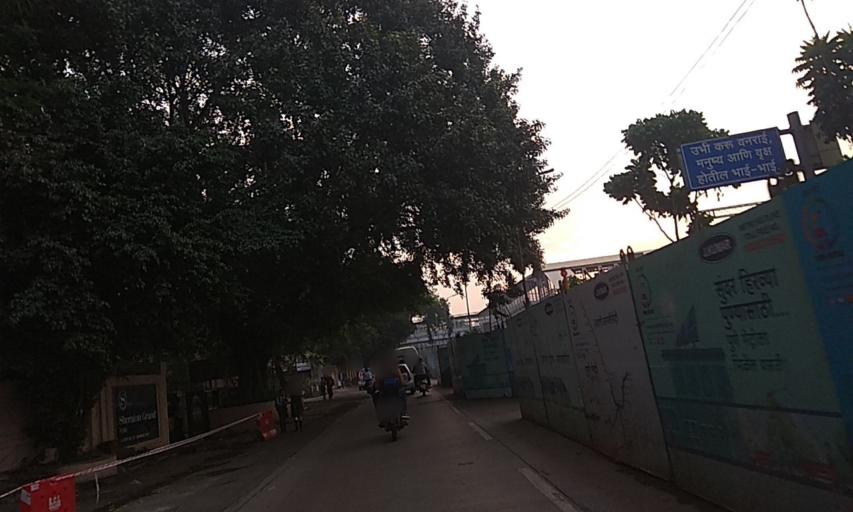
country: IN
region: Maharashtra
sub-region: Pune Division
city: Shivaji Nagar
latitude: 18.5297
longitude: 73.8716
